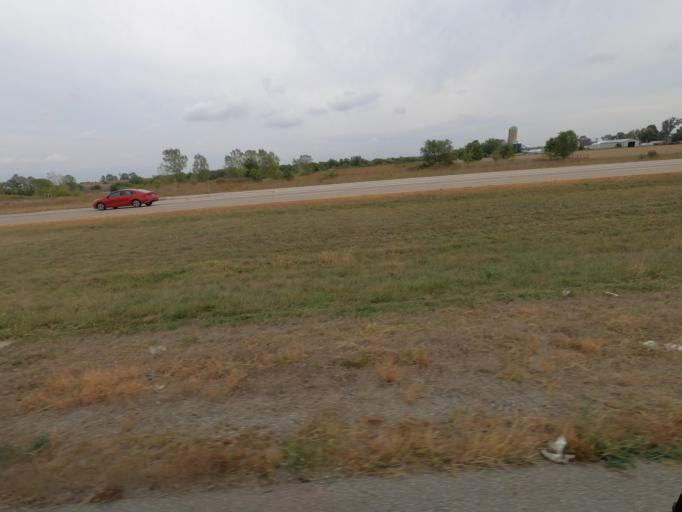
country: US
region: Iowa
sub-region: Jasper County
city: Monroe
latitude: 41.5405
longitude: -93.1303
